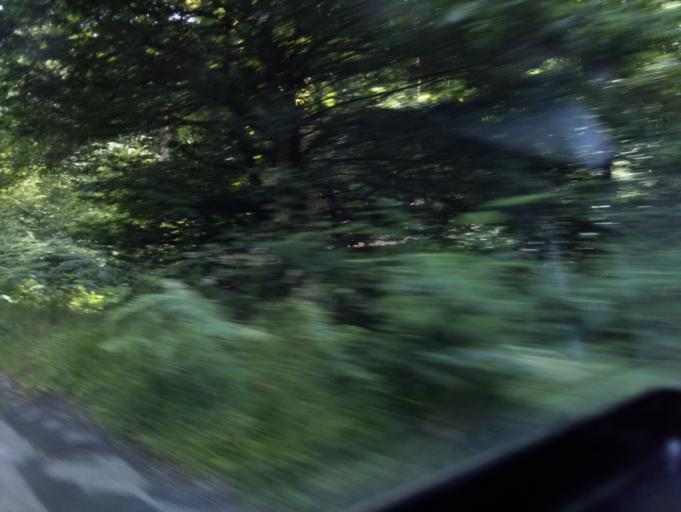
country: GB
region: England
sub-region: Gloucestershire
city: Cinderford
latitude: 51.7789
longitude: -2.5017
